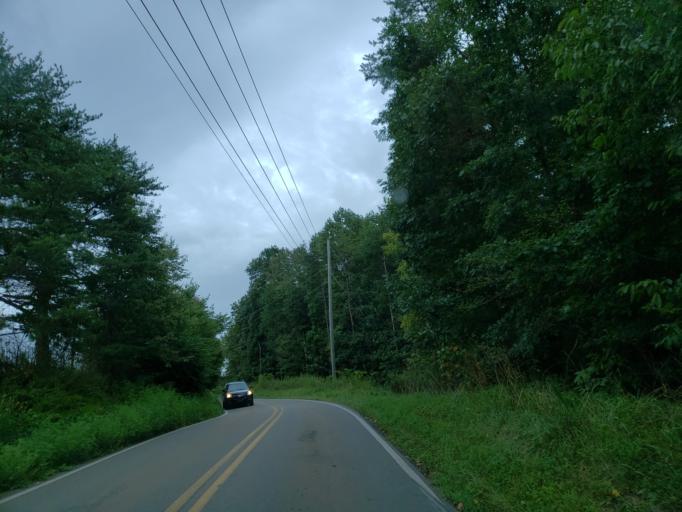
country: US
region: Georgia
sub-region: Pickens County
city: Jasper
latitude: 34.4259
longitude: -84.5467
